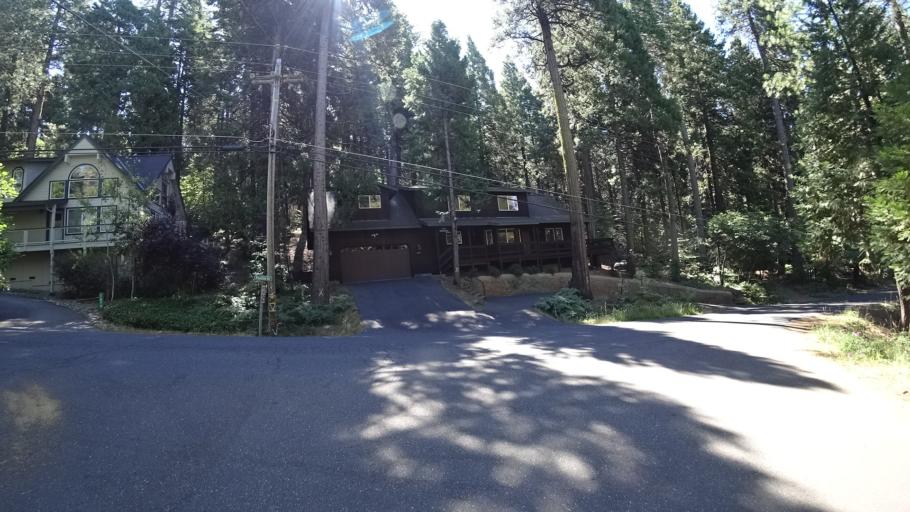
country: US
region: California
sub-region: Calaveras County
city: Arnold
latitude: 38.2519
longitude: -120.3278
